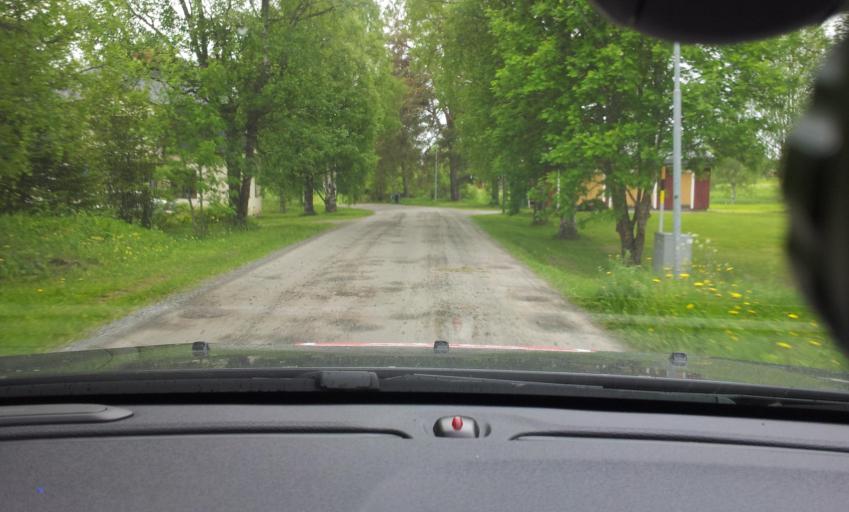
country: SE
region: Jaemtland
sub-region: OEstersunds Kommun
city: Ostersund
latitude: 62.9880
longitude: 14.5942
